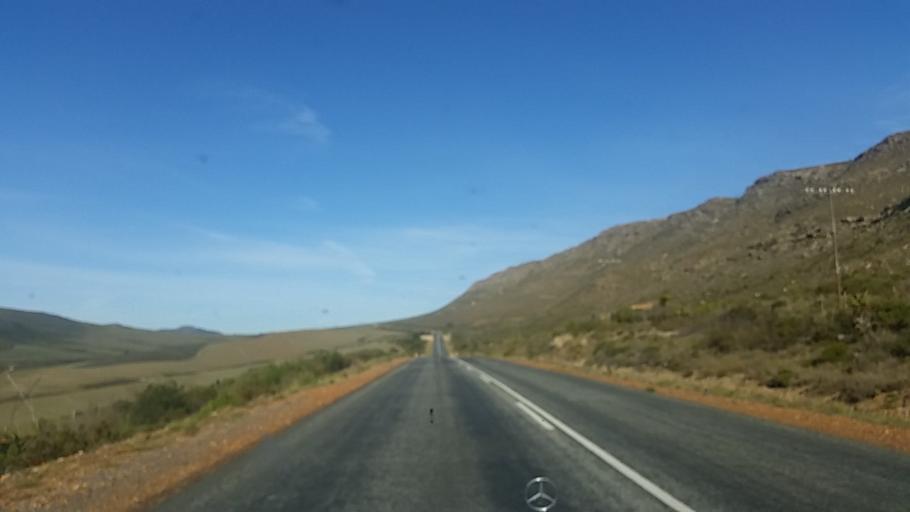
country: ZA
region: Western Cape
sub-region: Eden District Municipality
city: Knysna
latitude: -33.7425
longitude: 23.0094
